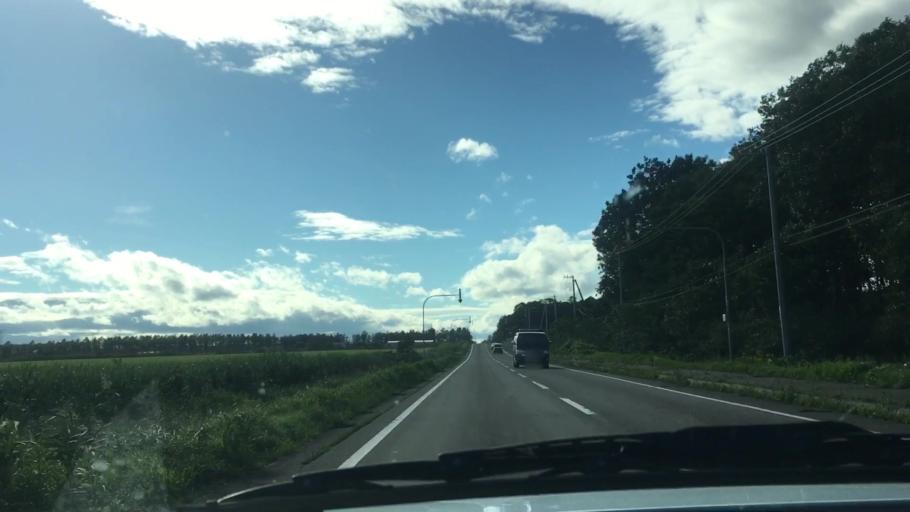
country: JP
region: Hokkaido
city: Otofuke
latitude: 43.1558
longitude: 143.1885
